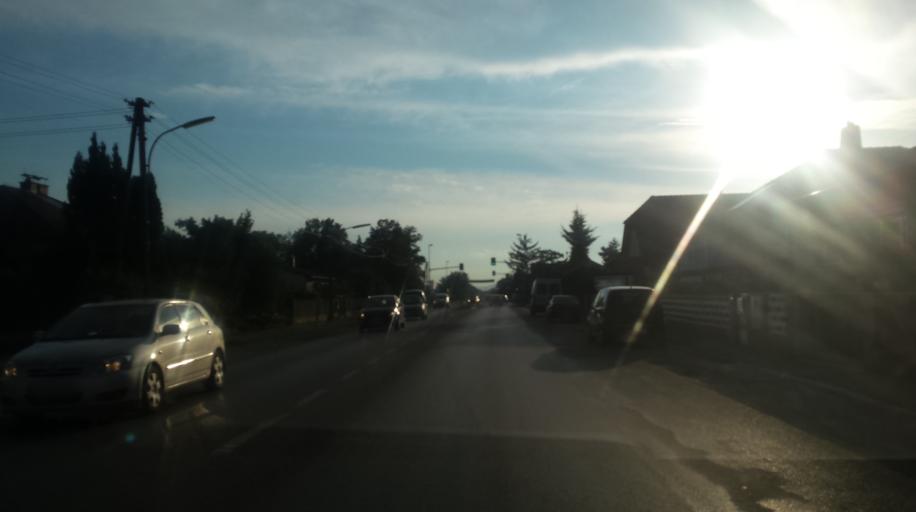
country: AT
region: Lower Austria
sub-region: Politischer Bezirk Ganserndorf
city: Parbasdorf
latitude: 48.3136
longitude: 16.6203
